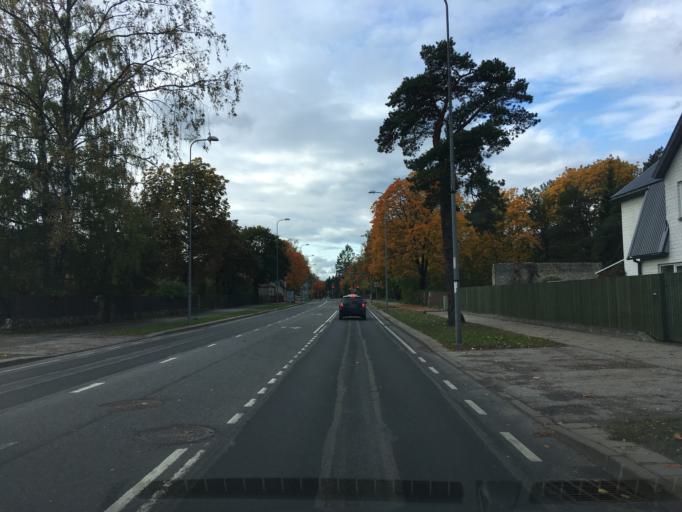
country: EE
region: Harju
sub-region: Saue vald
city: Laagri
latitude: 59.3793
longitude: 24.6569
